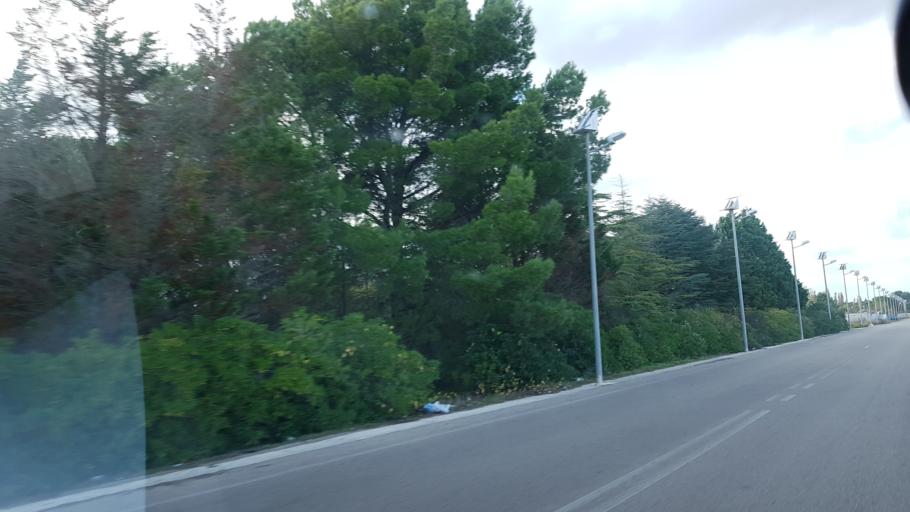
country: IT
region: Apulia
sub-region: Provincia di Brindisi
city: San Pietro Vernotico
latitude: 40.4945
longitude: 18.0082
